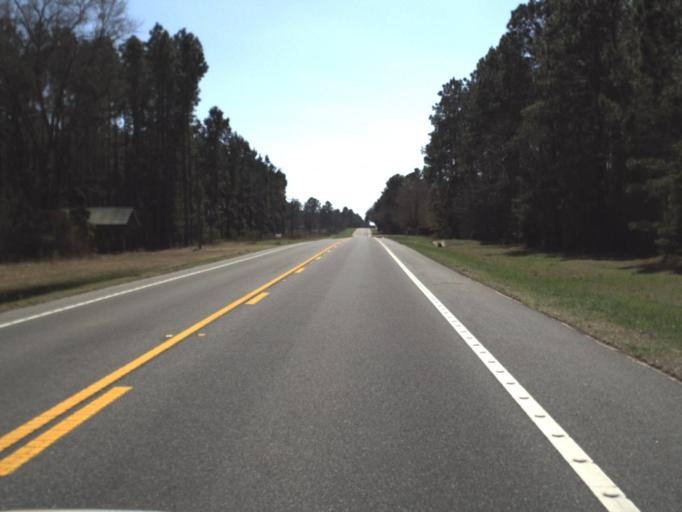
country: US
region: Florida
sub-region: Jackson County
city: Sneads
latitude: 30.6248
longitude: -85.0297
